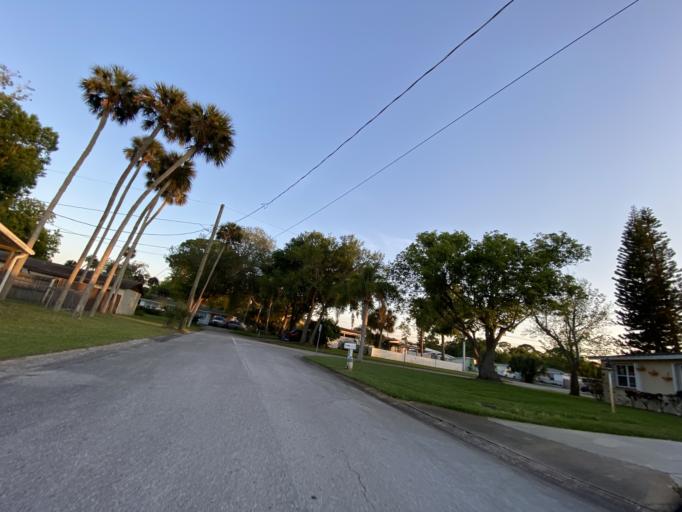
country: US
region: Florida
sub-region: Volusia County
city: South Daytona
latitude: 29.1774
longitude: -81.0075
